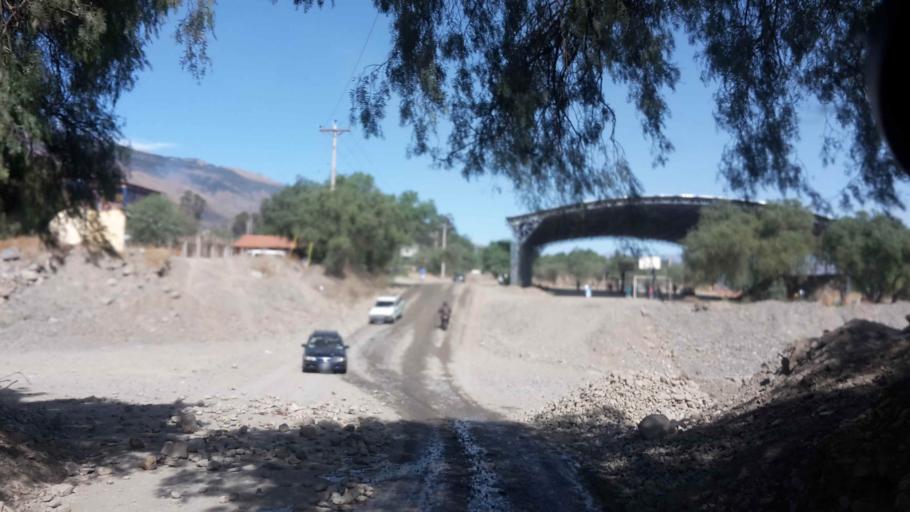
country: BO
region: Cochabamba
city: Cochabamba
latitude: -17.3386
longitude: -66.2135
